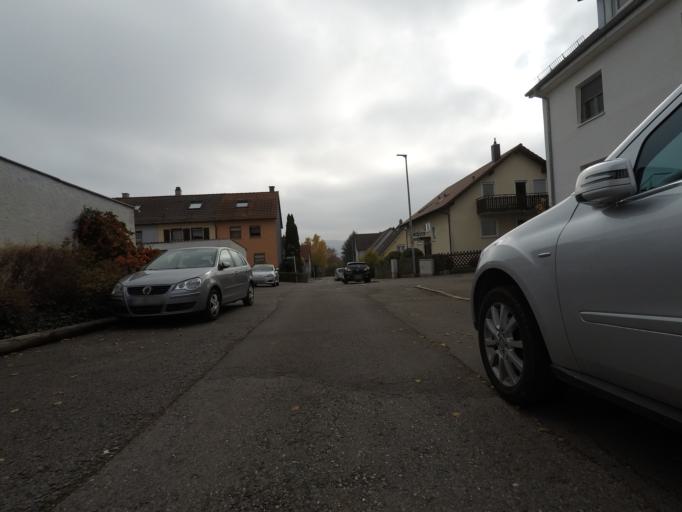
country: DE
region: Baden-Wuerttemberg
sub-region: Tuebingen Region
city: Reutlingen
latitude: 48.5061
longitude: 9.1995
